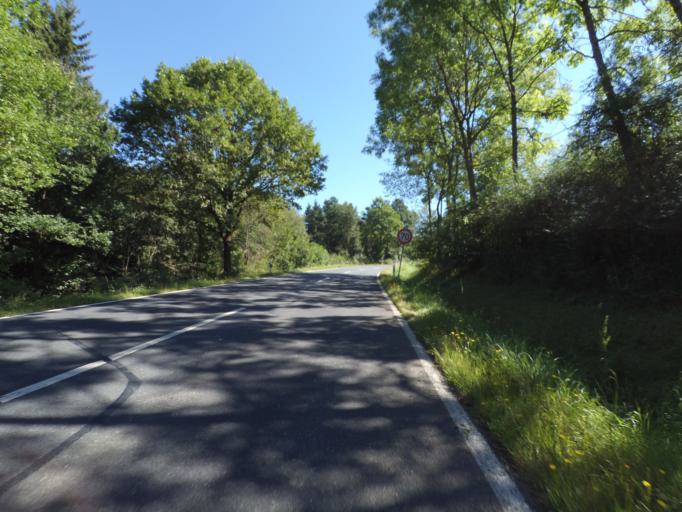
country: DE
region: Rheinland-Pfalz
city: Gefell
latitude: 50.2182
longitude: 6.9076
